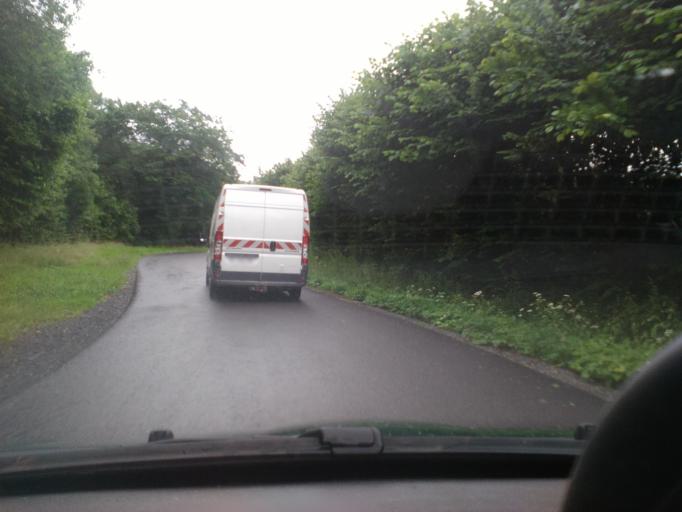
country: FR
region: Lorraine
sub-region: Departement des Vosges
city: Moyenmoutier
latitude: 48.3733
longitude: 6.9130
